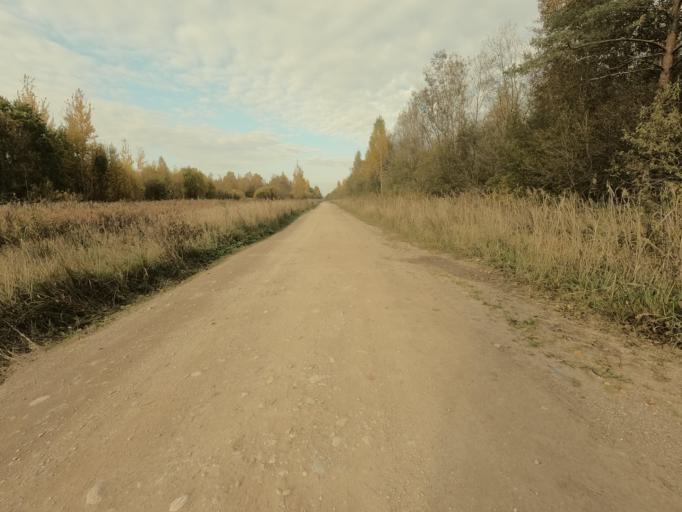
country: RU
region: Novgorod
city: Volkhovskiy
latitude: 58.9117
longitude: 31.0403
